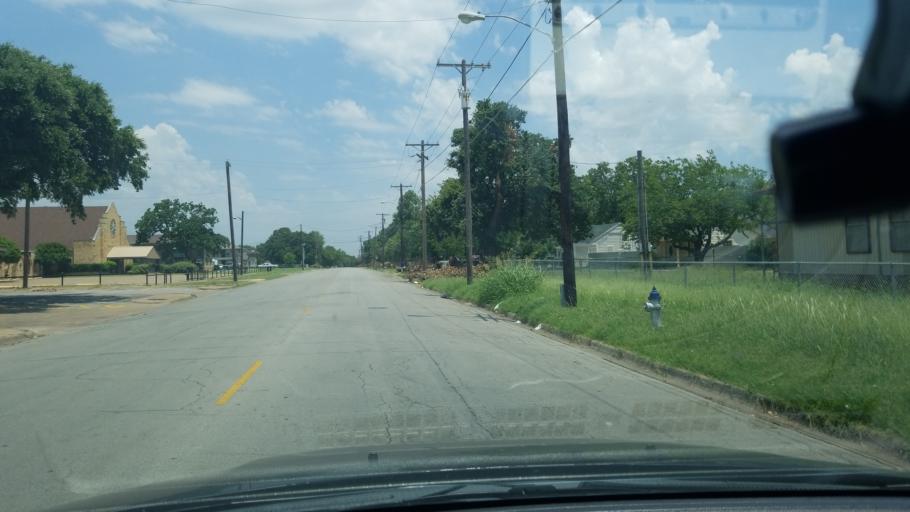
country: US
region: Texas
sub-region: Dallas County
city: Balch Springs
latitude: 32.7353
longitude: -96.6810
